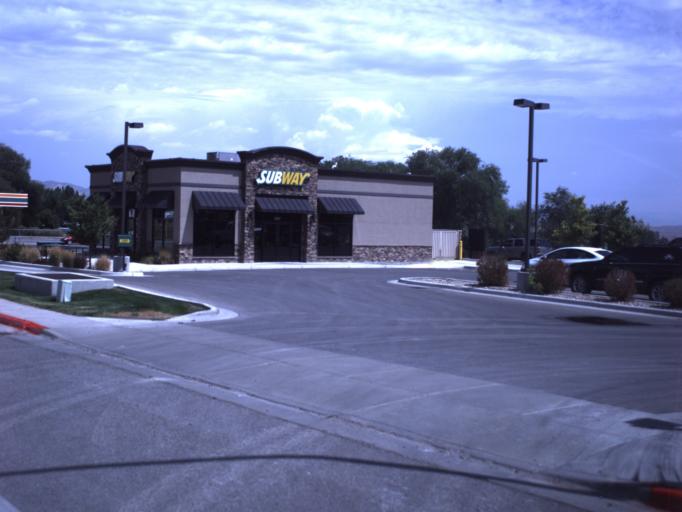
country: US
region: Utah
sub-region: Uintah County
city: Naples
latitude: 40.4188
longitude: -109.4992
